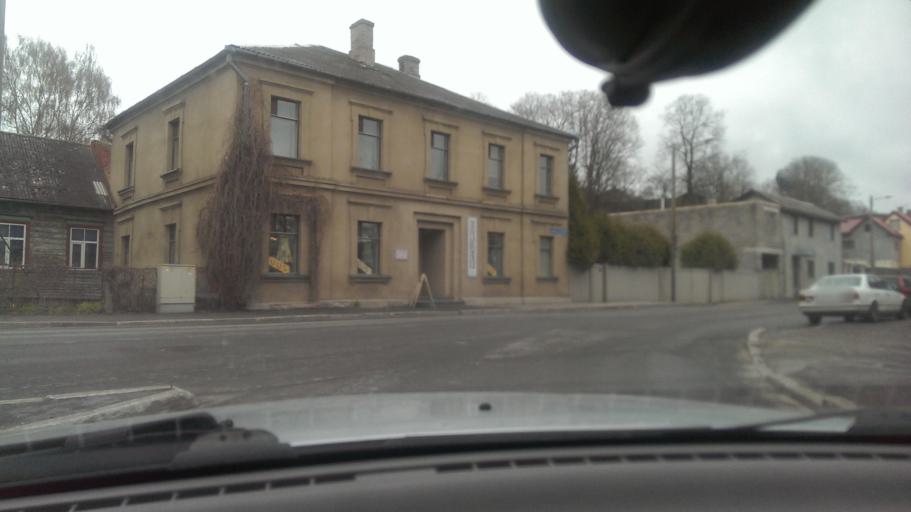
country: EE
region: Tartu
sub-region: Tartu linn
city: Tartu
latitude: 58.3876
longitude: 26.7271
